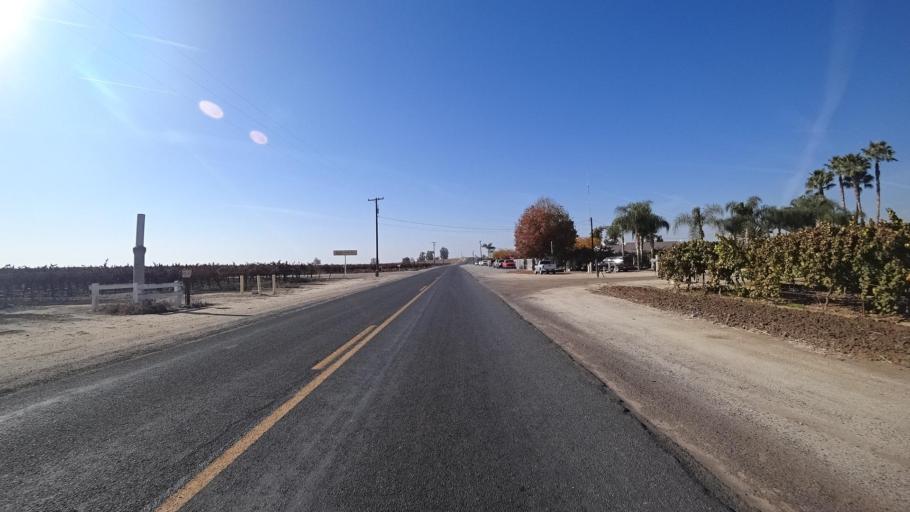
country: US
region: California
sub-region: Kern County
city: McFarland
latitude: 35.6455
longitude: -119.2131
